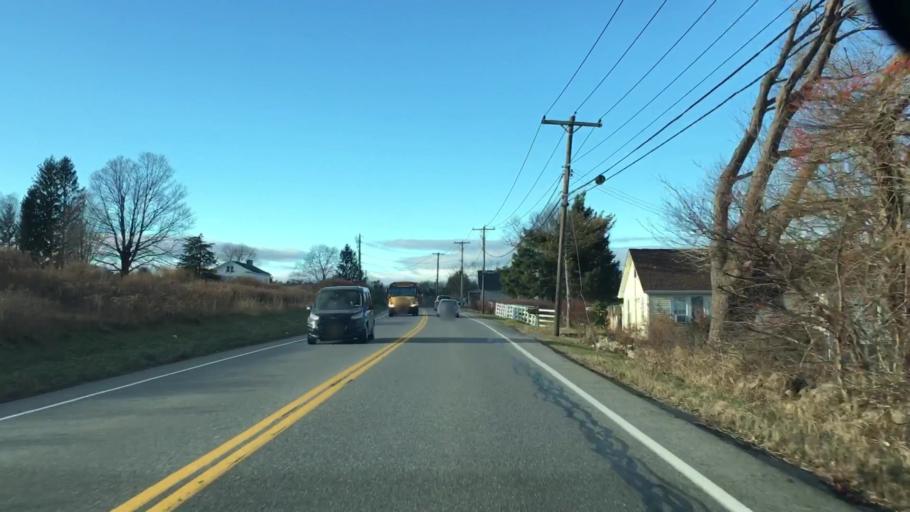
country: US
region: New York
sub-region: Putnam County
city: Carmel
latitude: 41.4299
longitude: -73.6513
